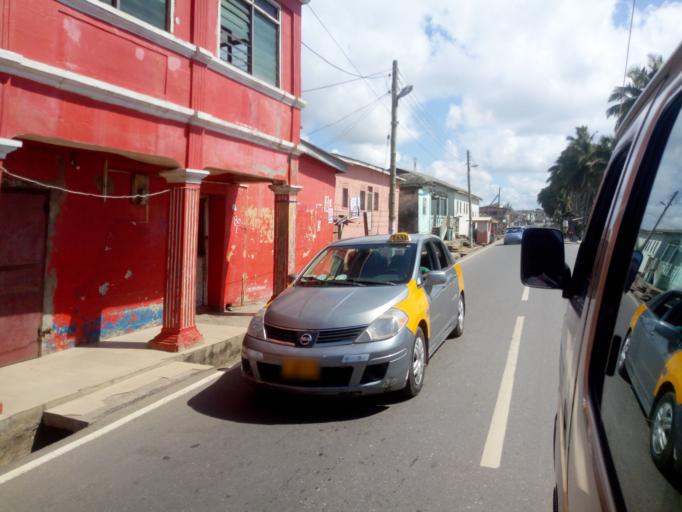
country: GH
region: Central
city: Elmina
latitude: 5.0888
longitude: -1.3479
